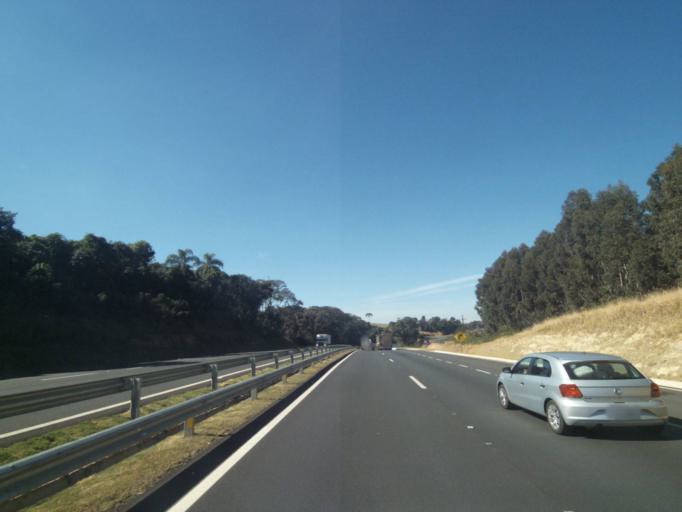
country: BR
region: Parana
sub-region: Tibagi
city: Tibagi
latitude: -24.8582
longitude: -50.4543
